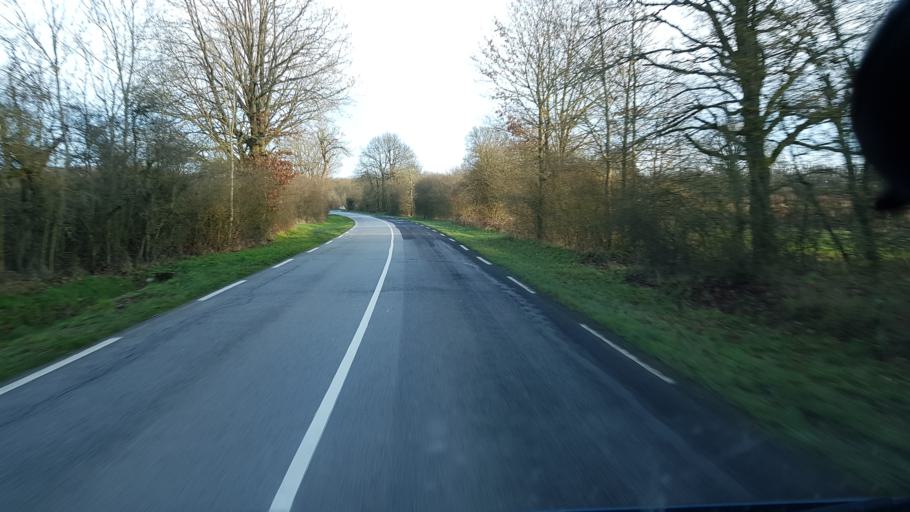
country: FR
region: Ile-de-France
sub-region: Departement des Yvelines
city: Auffargis
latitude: 48.6704
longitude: 1.9206
